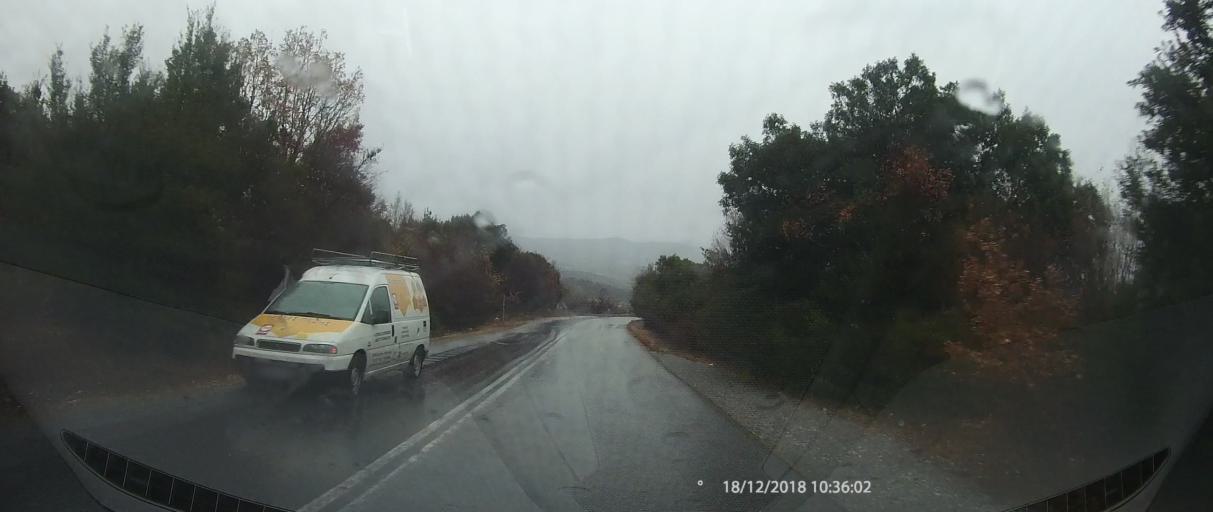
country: GR
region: Central Macedonia
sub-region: Nomos Pierias
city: Kato Milia
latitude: 40.2154
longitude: 22.3093
